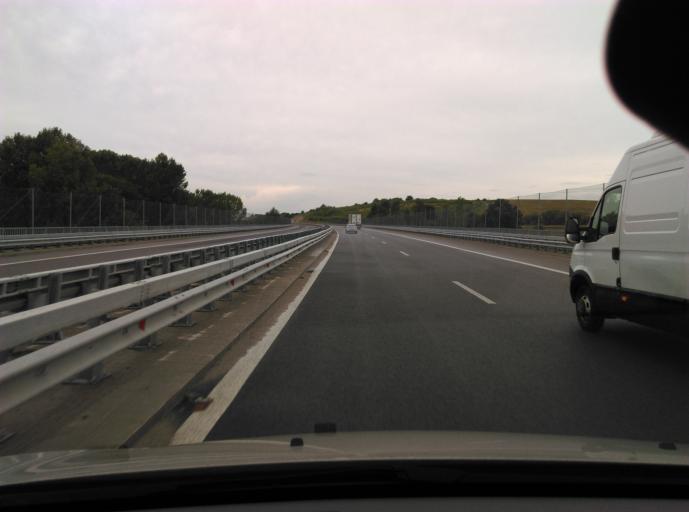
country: BG
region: Stara Zagora
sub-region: Obshtina Chirpan
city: Chirpan
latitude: 42.0921
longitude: 25.4469
